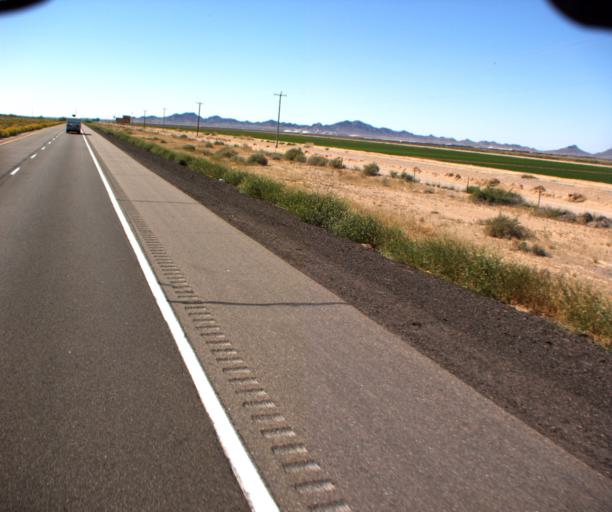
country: US
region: Arizona
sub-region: Maricopa County
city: Gila Bend
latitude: 32.9142
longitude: -112.9403
